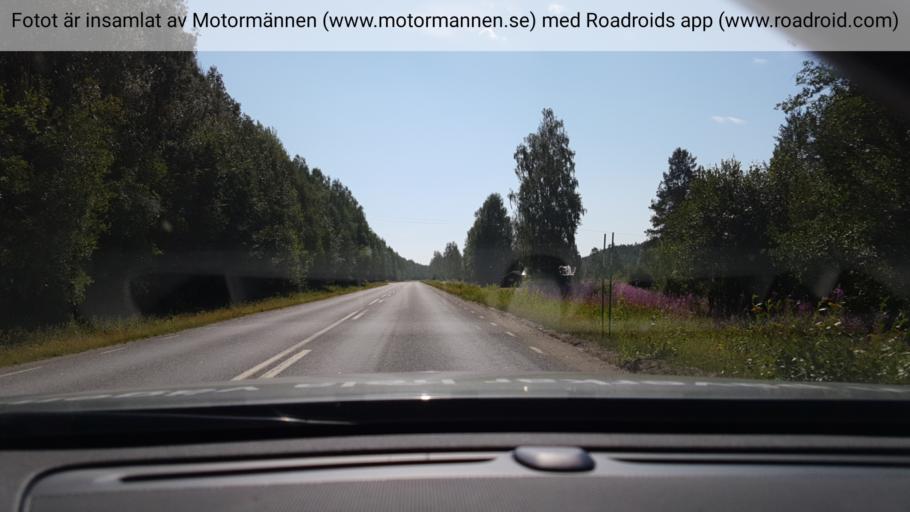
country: SE
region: Vaesterbotten
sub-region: Vindelns Kommun
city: Vindeln
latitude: 64.3097
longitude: 19.6087
